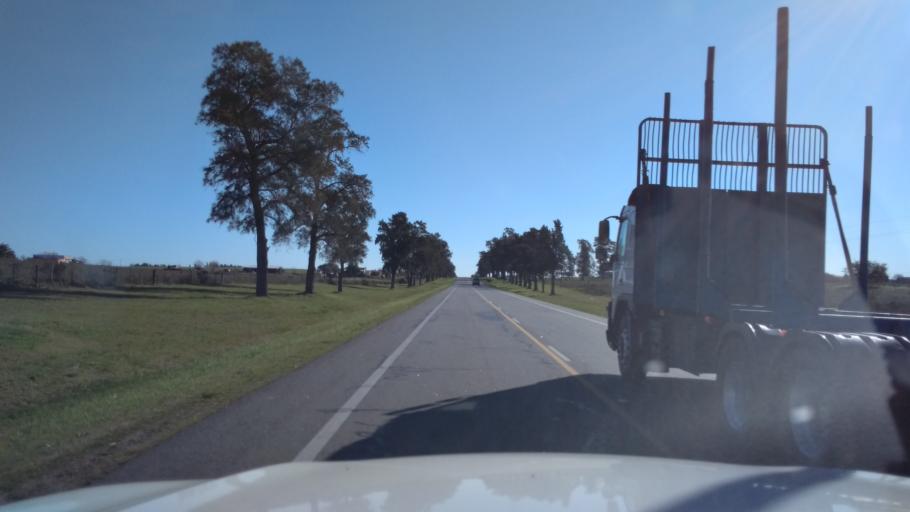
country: UY
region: Canelones
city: San Jacinto
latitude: -34.5405
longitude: -55.8943
